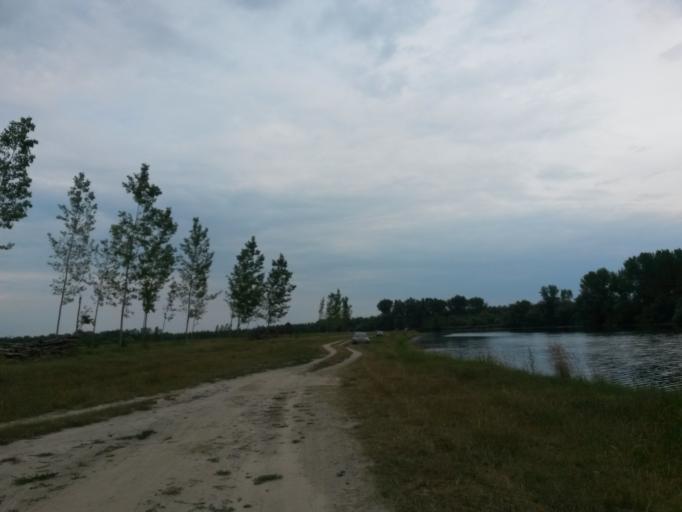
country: HR
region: Osjecko-Baranjska
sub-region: Grad Osijek
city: Bilje
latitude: 45.5901
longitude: 18.7419
